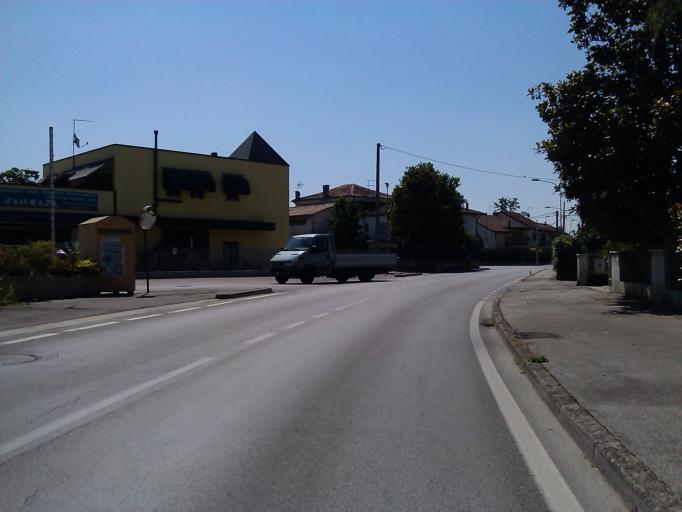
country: IT
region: Veneto
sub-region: Provincia di Treviso
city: Loria Bessica
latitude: 45.7312
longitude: 11.8591
